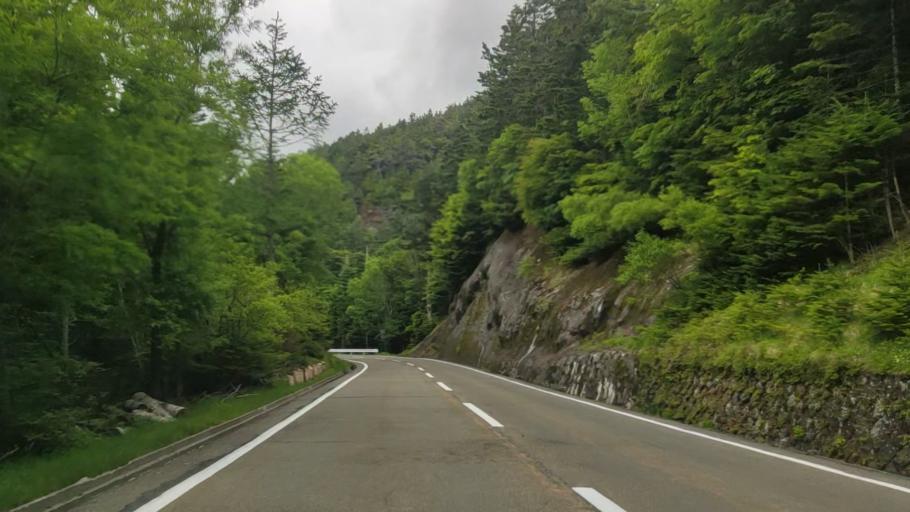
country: JP
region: Yamanashi
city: Fujikawaguchiko
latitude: 35.4002
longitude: 138.6934
